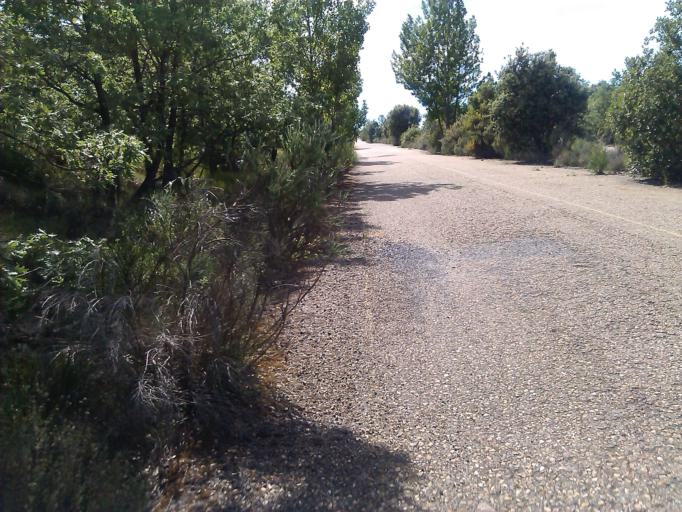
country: ES
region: Castille and Leon
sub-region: Provincia de Leon
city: San Justo de la Vega
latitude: 42.4478
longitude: -5.9743
